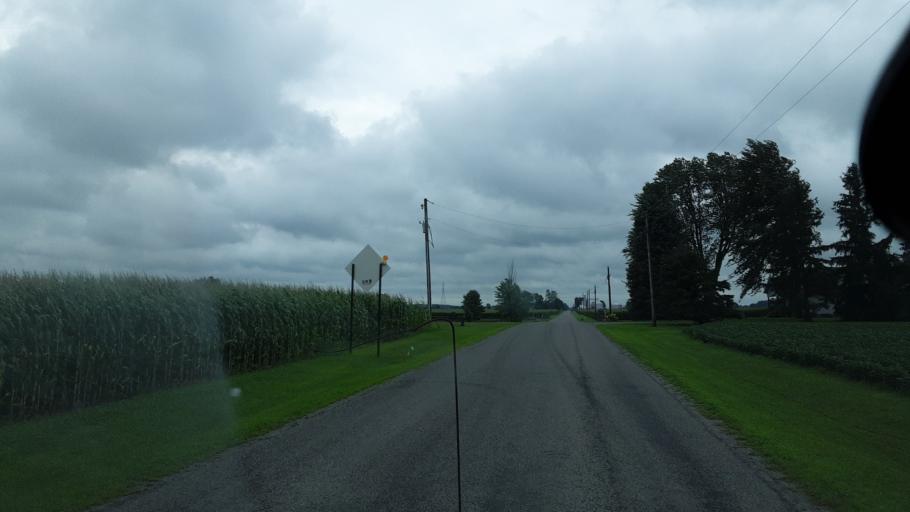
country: US
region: Indiana
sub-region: Wells County
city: Ossian
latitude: 40.9310
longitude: -85.1099
